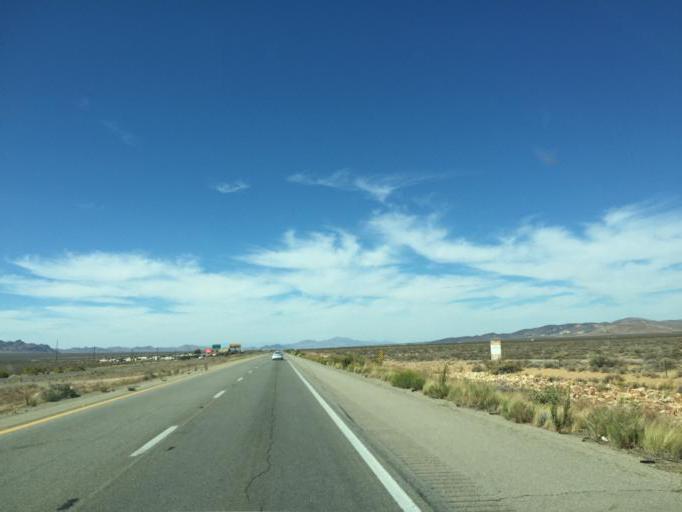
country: US
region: Arizona
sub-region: Mohave County
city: Dolan Springs
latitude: 35.5540
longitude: -114.3691
